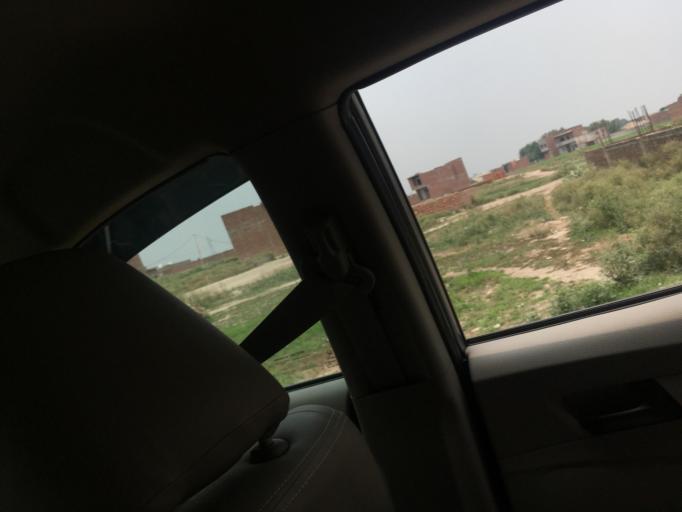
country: PK
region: Punjab
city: Lahore
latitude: 31.6165
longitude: 74.3554
